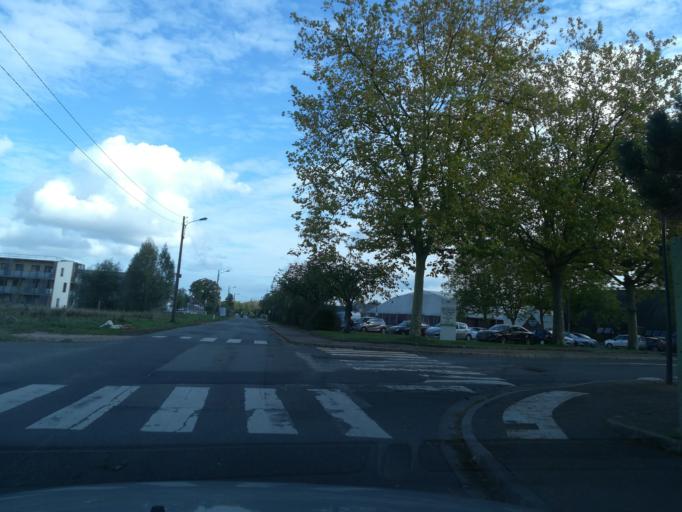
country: FR
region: Haute-Normandie
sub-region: Departement de la Seine-Maritime
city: Bois-Guillaume
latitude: 49.4731
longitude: 1.1268
